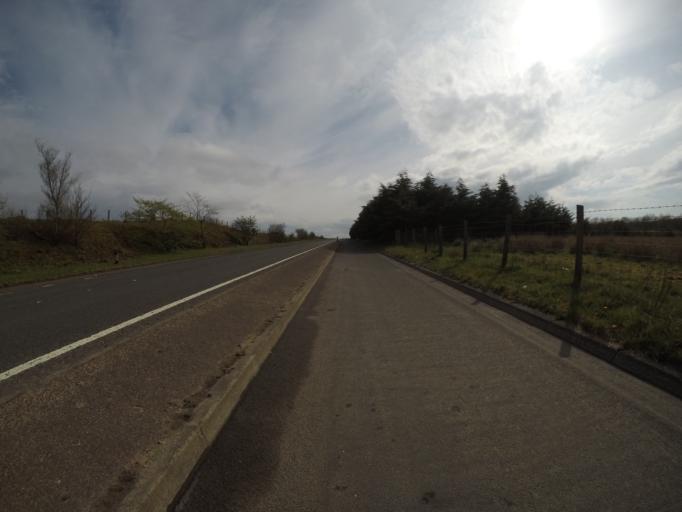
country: GB
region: Scotland
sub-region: East Renfrewshire
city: Newton Mearns
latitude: 55.7328
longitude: -4.3813
